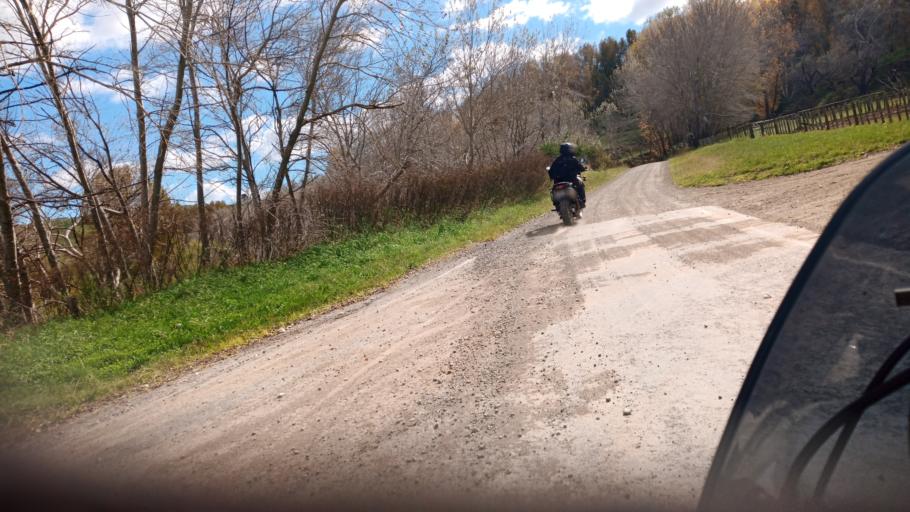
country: NZ
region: Gisborne
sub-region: Gisborne District
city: Gisborne
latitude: -38.4252
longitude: 177.7235
